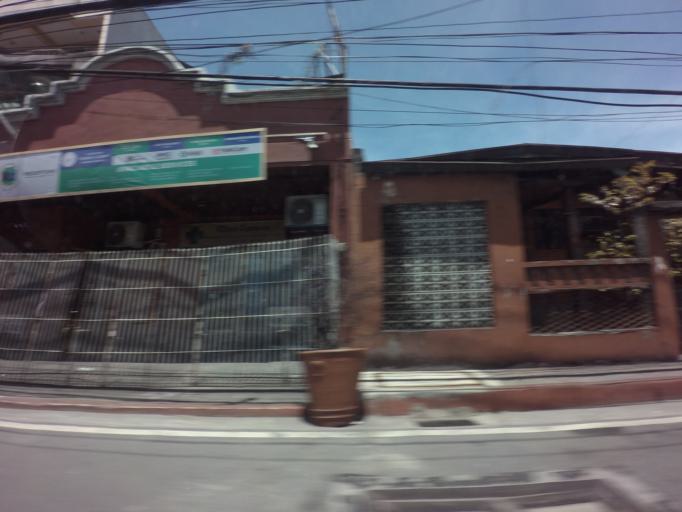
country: PH
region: Calabarzon
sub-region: Province of Rizal
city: Las Pinas
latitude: 14.4801
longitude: 120.9807
